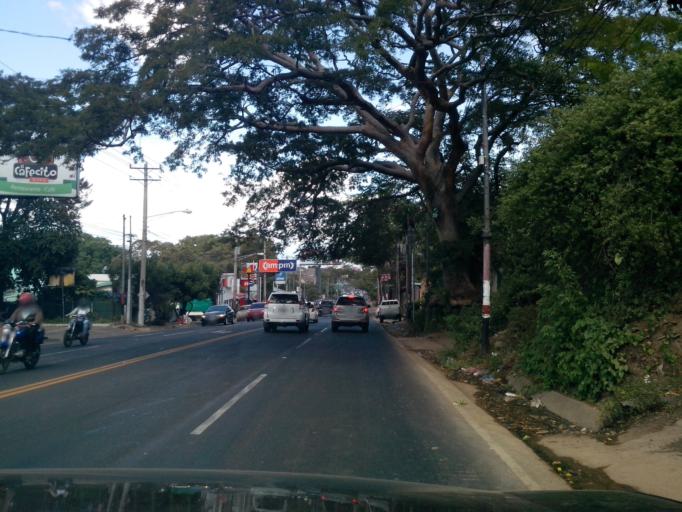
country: NI
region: Managua
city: Ciudad Sandino
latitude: 12.1178
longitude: -86.3150
